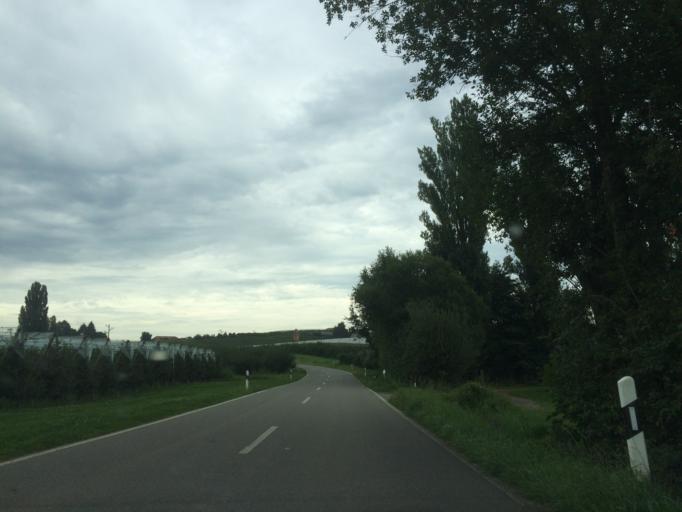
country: DE
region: Baden-Wuerttemberg
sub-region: Tuebingen Region
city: Immenstaad am Bodensee
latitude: 47.6704
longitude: 9.3420
